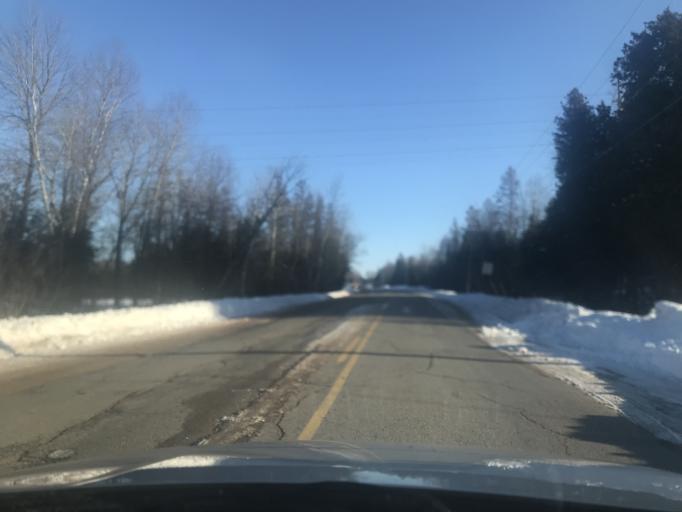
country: US
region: Wisconsin
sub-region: Marinette County
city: Marinette
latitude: 45.1449
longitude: -87.6540
